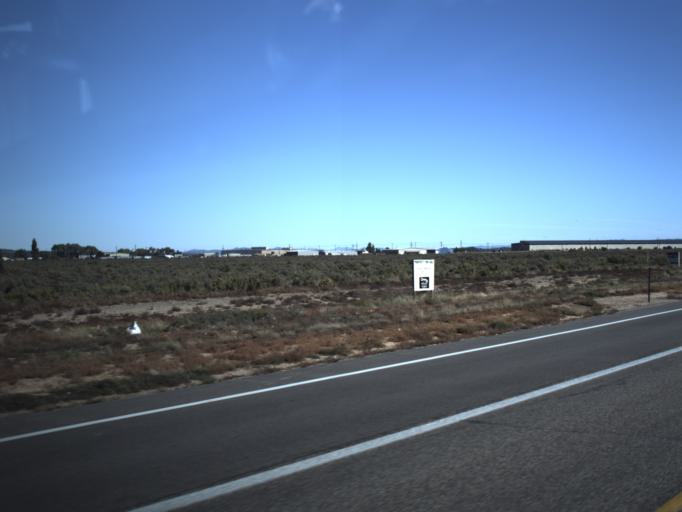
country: US
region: Utah
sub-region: Iron County
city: Cedar City
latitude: 37.6802
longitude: -113.1715
